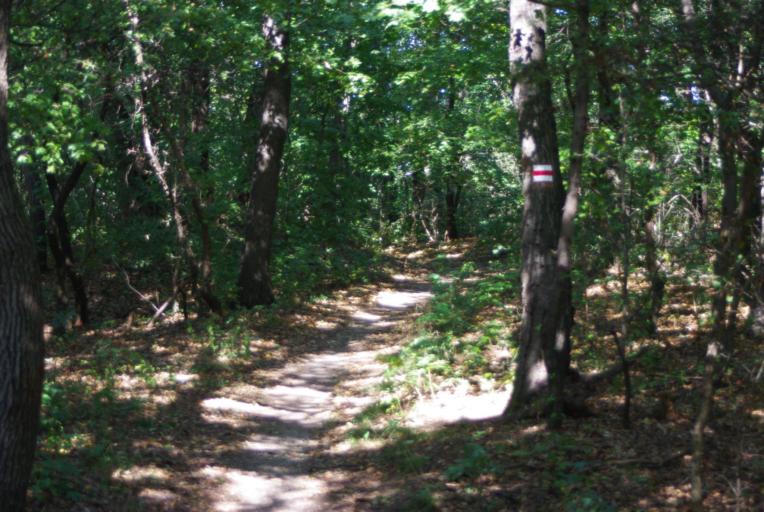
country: HU
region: Pest
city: Toeroekbalint
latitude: 47.4238
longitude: 18.9088
